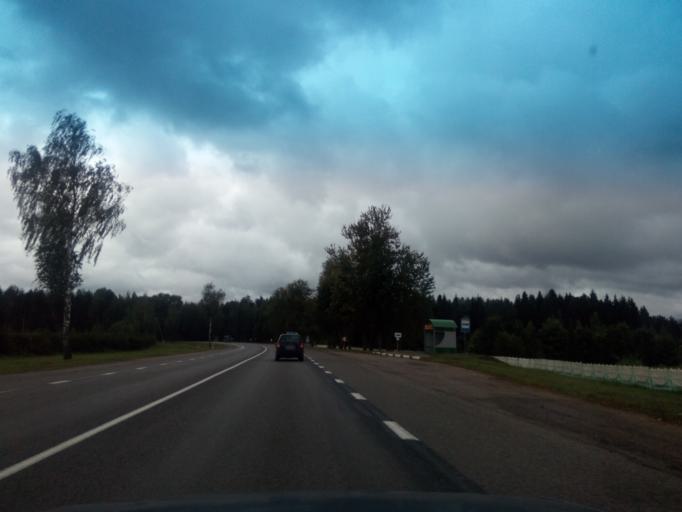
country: BY
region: Vitebsk
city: Lyepyel'
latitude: 54.8910
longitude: 28.7381
